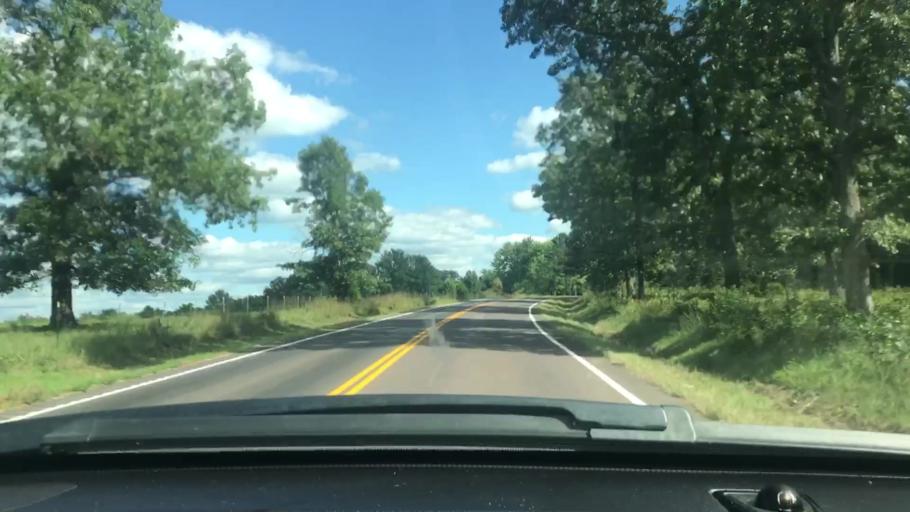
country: US
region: Missouri
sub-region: Wright County
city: Mountain Grove
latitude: 37.2312
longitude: -92.2955
